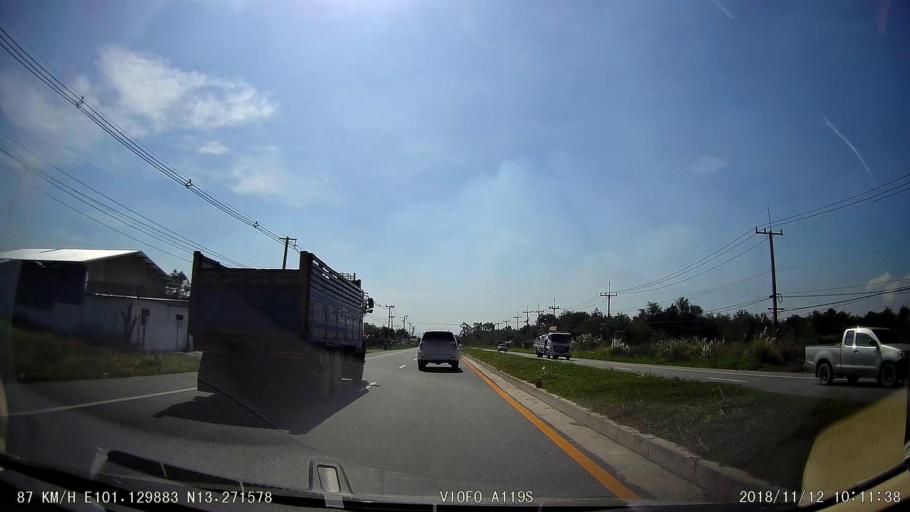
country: TH
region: Chon Buri
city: Ban Bueng
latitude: 13.2713
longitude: 101.1300
